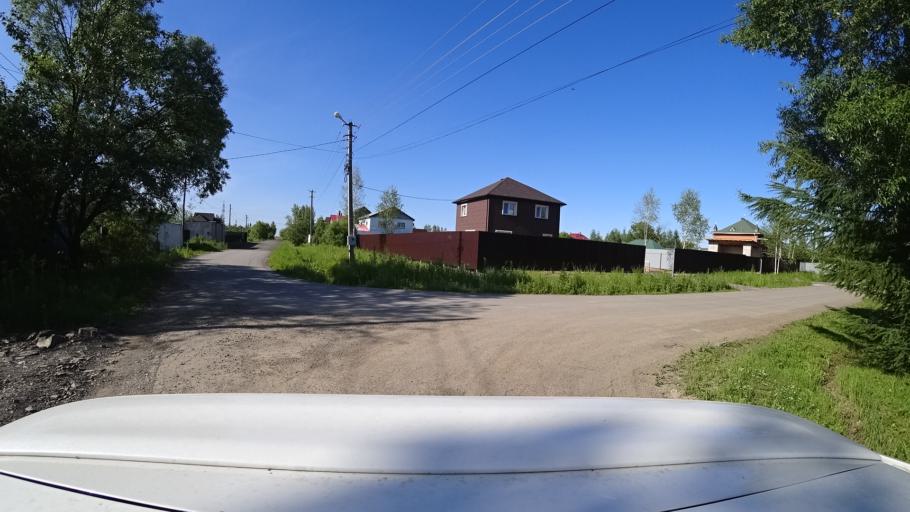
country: RU
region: Khabarovsk Krai
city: Topolevo
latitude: 48.5503
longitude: 135.1692
